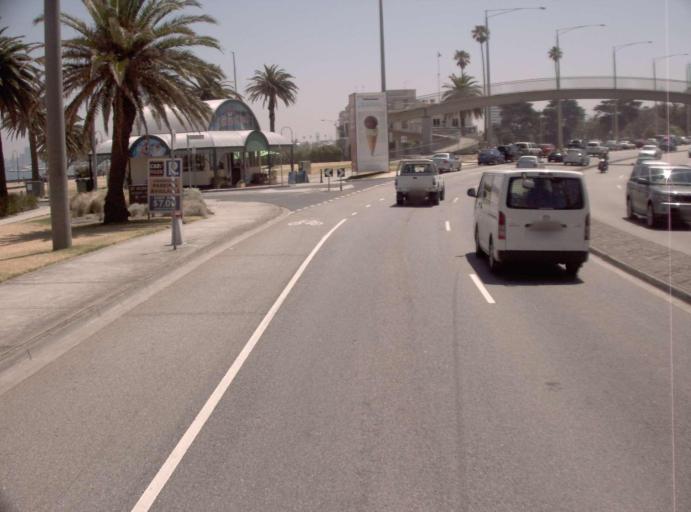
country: AU
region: Victoria
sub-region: Port Phillip
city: St Kilda West
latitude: -37.8647
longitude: 144.9723
